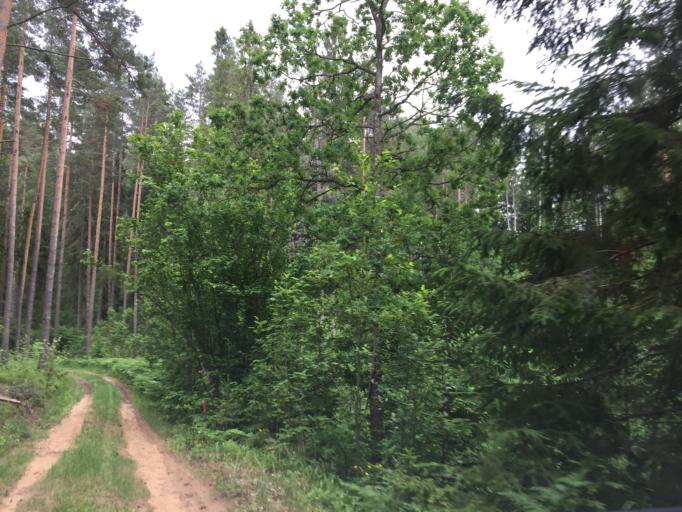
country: LV
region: Tukuma Rajons
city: Tukums
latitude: 57.0301
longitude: 23.0753
